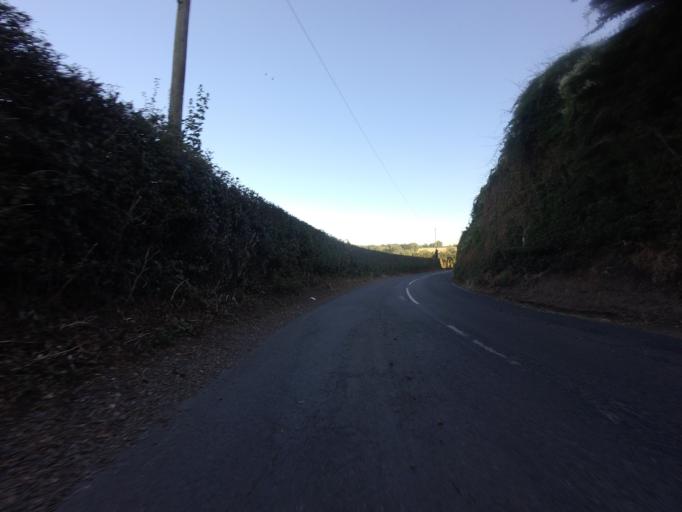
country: GB
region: England
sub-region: Kent
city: Herne Bay
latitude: 51.3315
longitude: 1.1899
